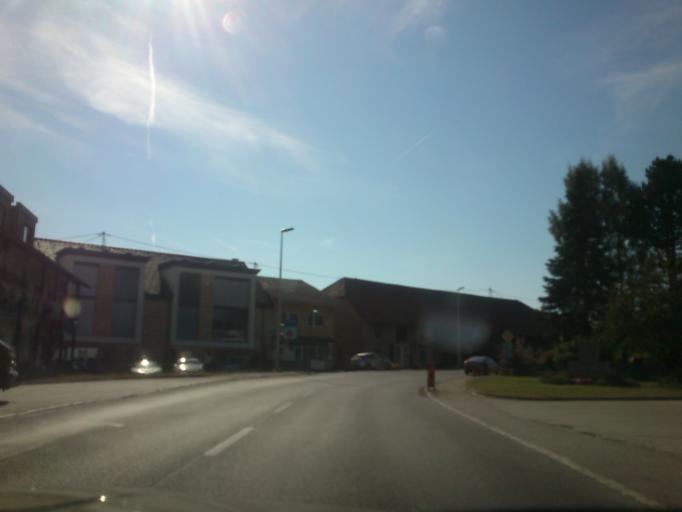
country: AT
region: Upper Austria
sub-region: Politischer Bezirk Freistadt
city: Freistadt
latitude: 48.5577
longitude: 14.4779
